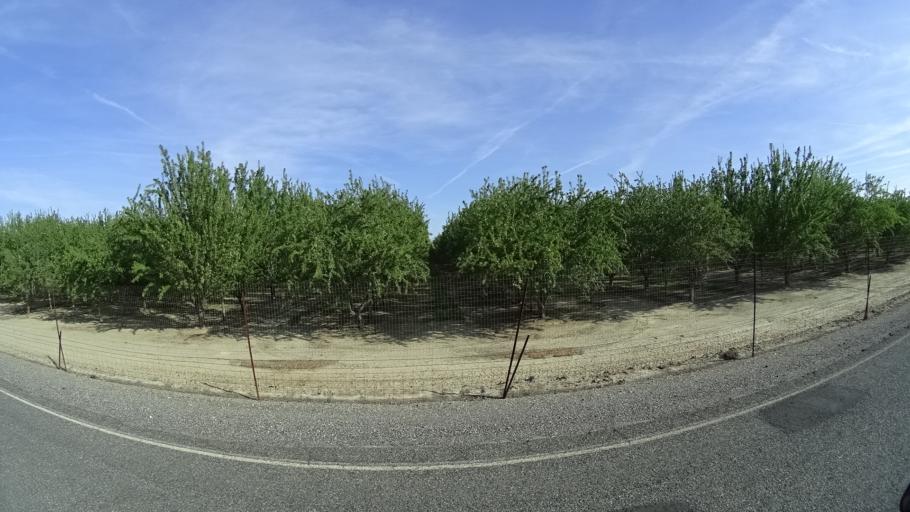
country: US
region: California
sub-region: Glenn County
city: Orland
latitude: 39.6679
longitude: -122.2147
